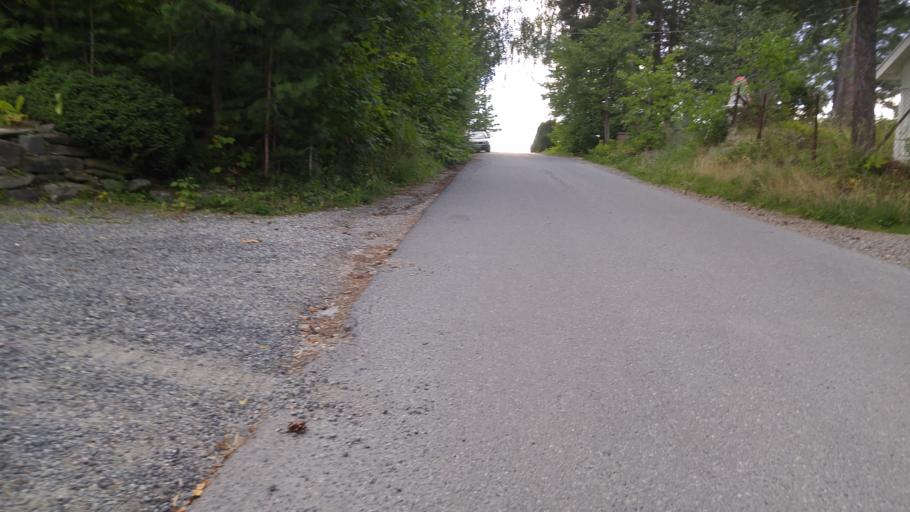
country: NO
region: Akershus
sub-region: Asker
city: Billingstad
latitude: 59.8478
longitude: 10.4916
